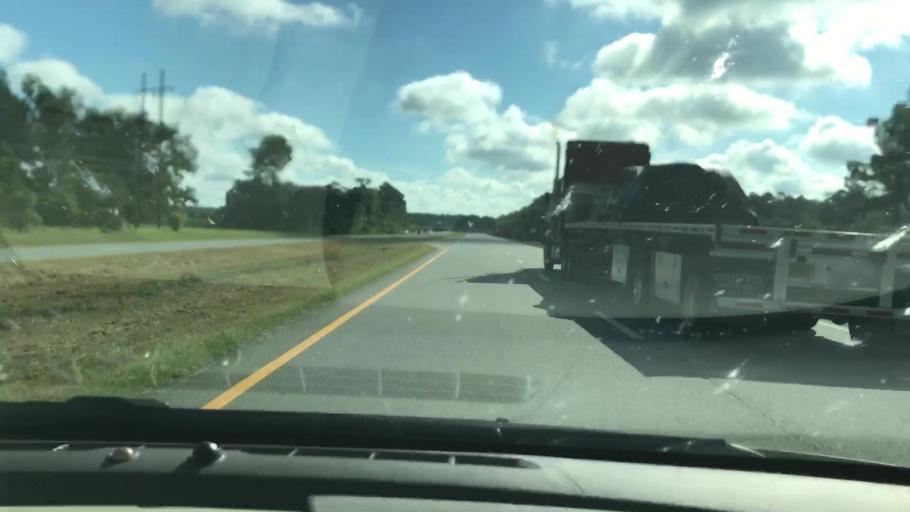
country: US
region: Georgia
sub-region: Worth County
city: Sylvester
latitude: 31.5507
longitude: -83.9593
